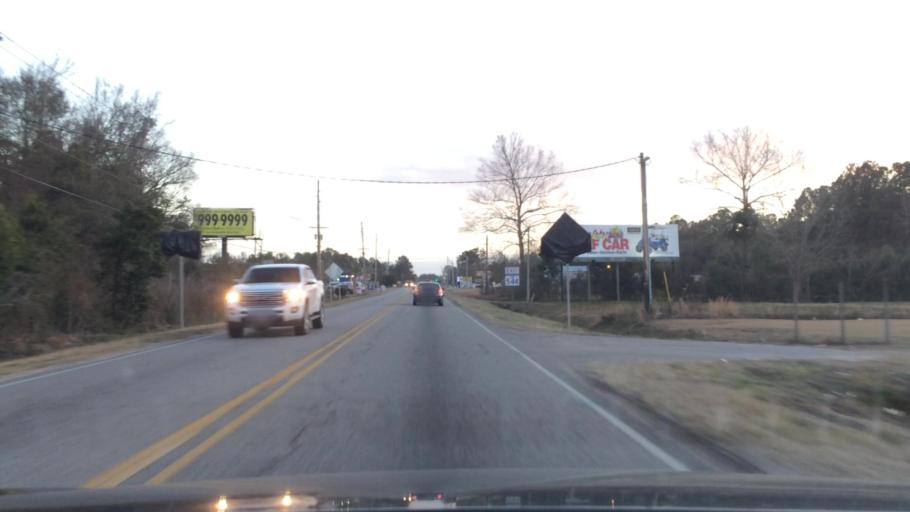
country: US
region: South Carolina
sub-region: Horry County
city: Red Hill
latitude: 33.8063
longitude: -79.0186
